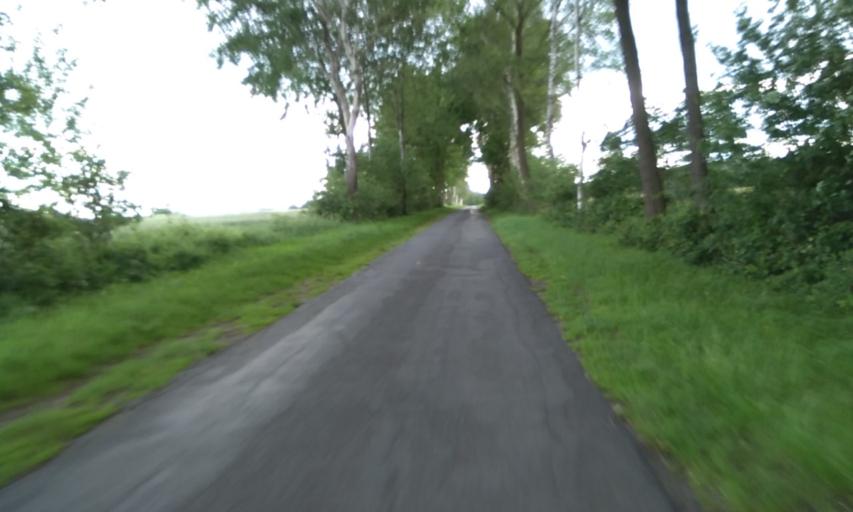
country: DE
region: Lower Saxony
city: Regesbostel
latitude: 53.3831
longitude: 9.6280
